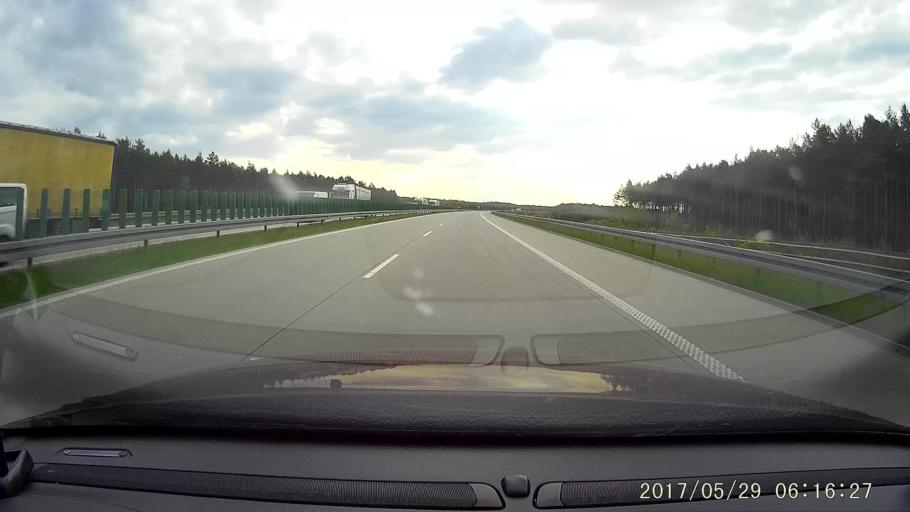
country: PL
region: Lower Silesian Voivodeship
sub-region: Powiat boleslawiecki
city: Nowogrodziec
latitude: 51.2672
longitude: 15.3746
